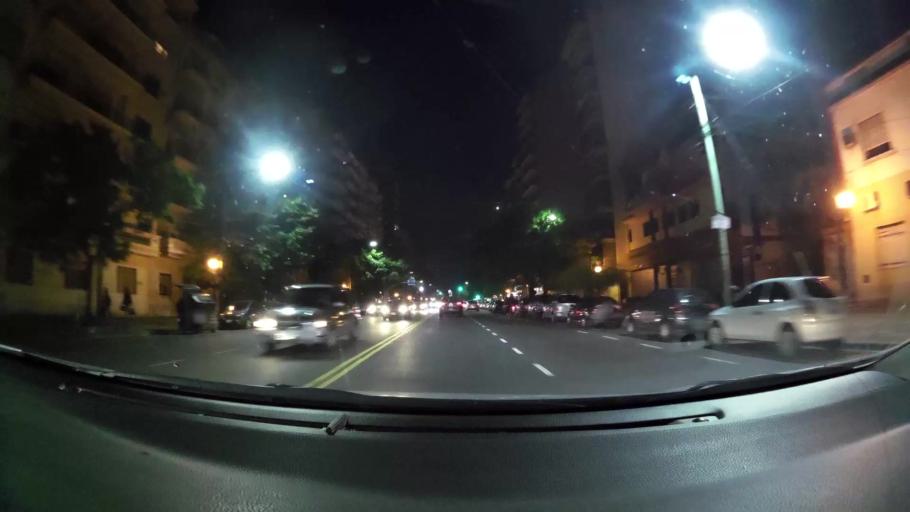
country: AR
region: Buenos Aires F.D.
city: Colegiales
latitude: -34.5685
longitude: -58.4580
